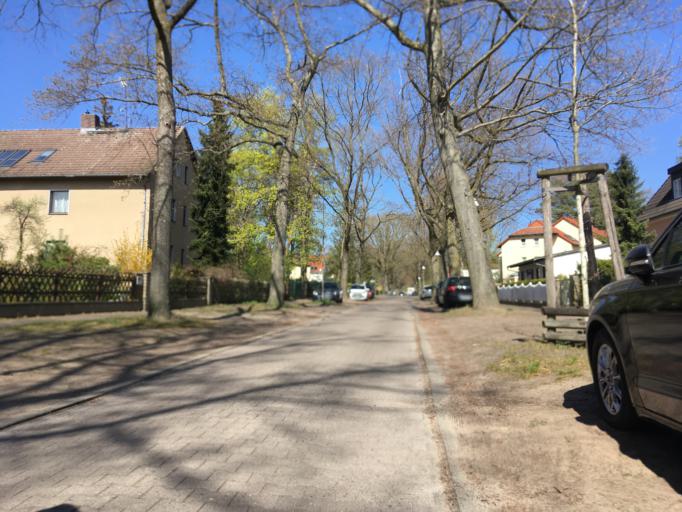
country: DE
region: Berlin
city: Hermsdorf
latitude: 52.6078
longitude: 13.2949
